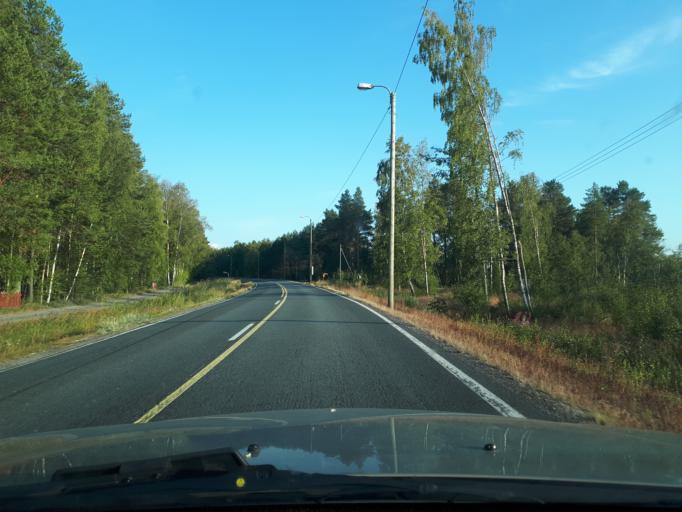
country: FI
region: Northern Ostrobothnia
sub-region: Oulu
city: Oulunsalo
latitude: 64.9888
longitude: 25.2581
